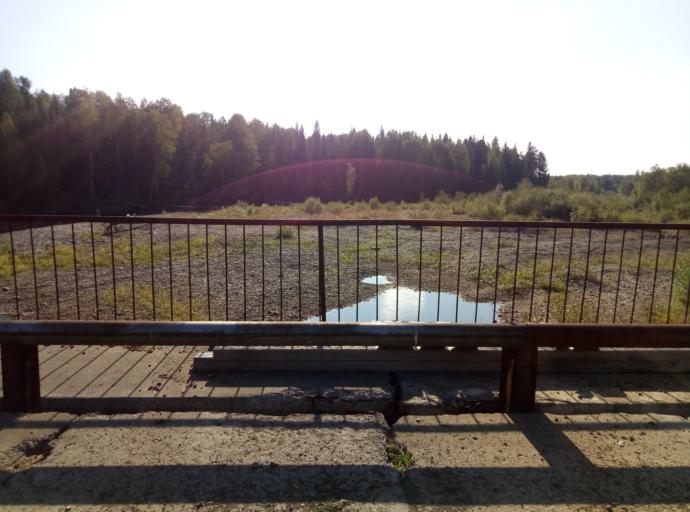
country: RU
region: Sverdlovsk
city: Karpinsk
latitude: 59.4986
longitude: 59.7591
